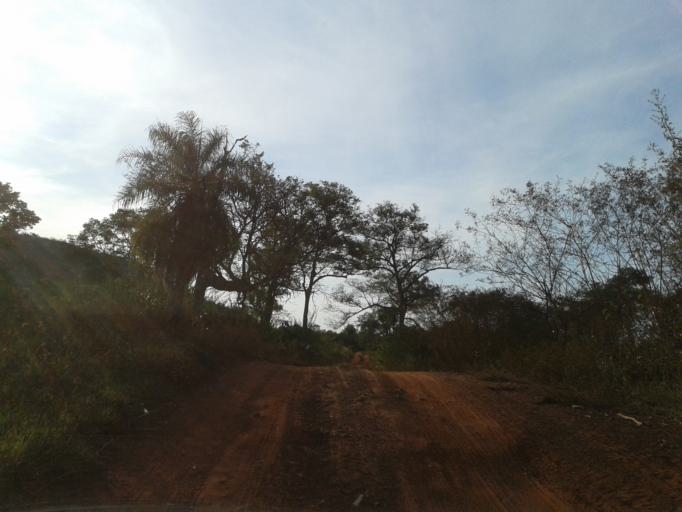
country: BR
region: Minas Gerais
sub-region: Campina Verde
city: Campina Verde
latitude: -19.4995
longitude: -49.6053
